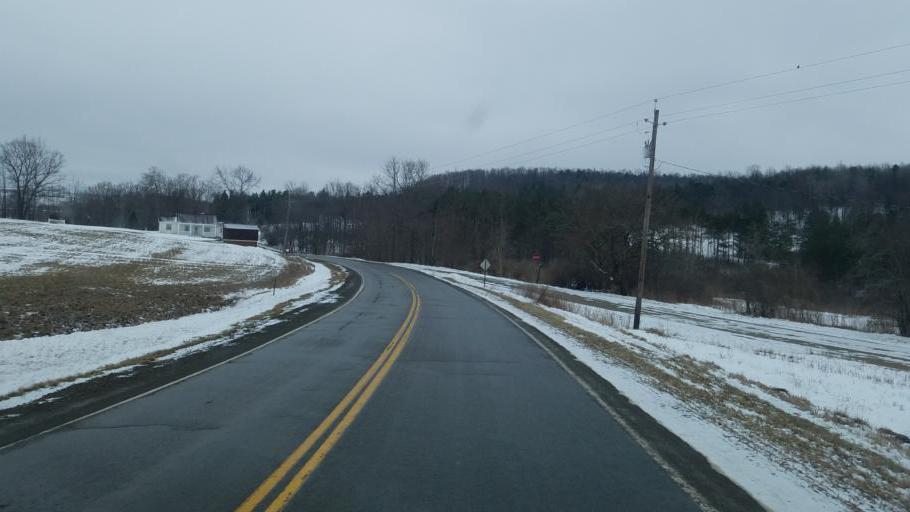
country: US
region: Pennsylvania
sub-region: Tioga County
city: Elkland
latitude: 42.1103
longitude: -77.4095
